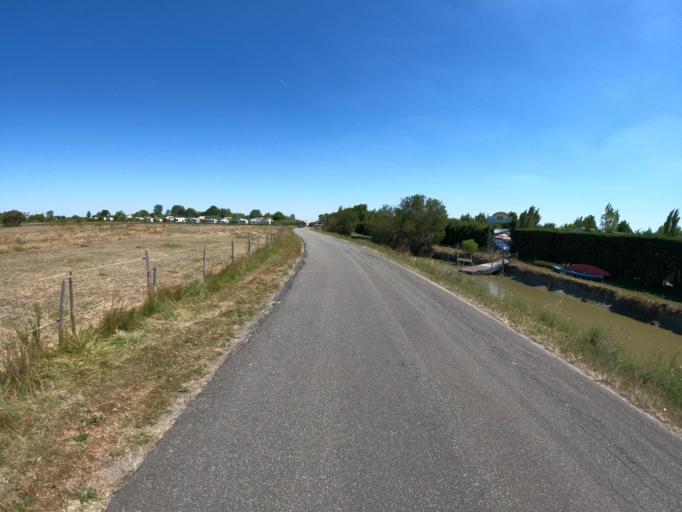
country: FR
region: Pays de la Loire
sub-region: Departement de la Vendee
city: Saint-Jean-de-Monts
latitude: 46.8009
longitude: -2.0724
